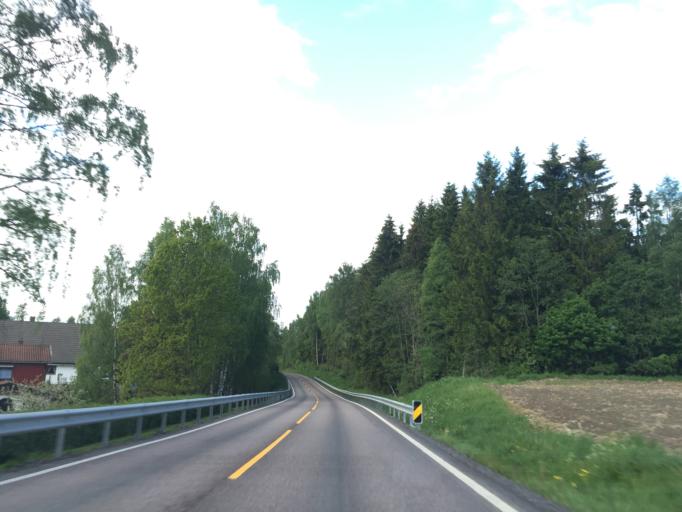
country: NO
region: Akershus
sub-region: Fet
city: Fetsund
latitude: 59.9460
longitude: 11.1970
